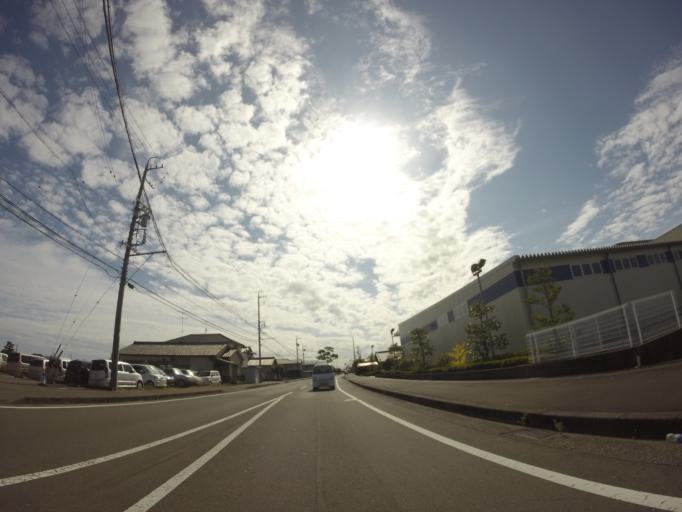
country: JP
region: Shizuoka
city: Fujieda
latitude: 34.8481
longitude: 138.2842
